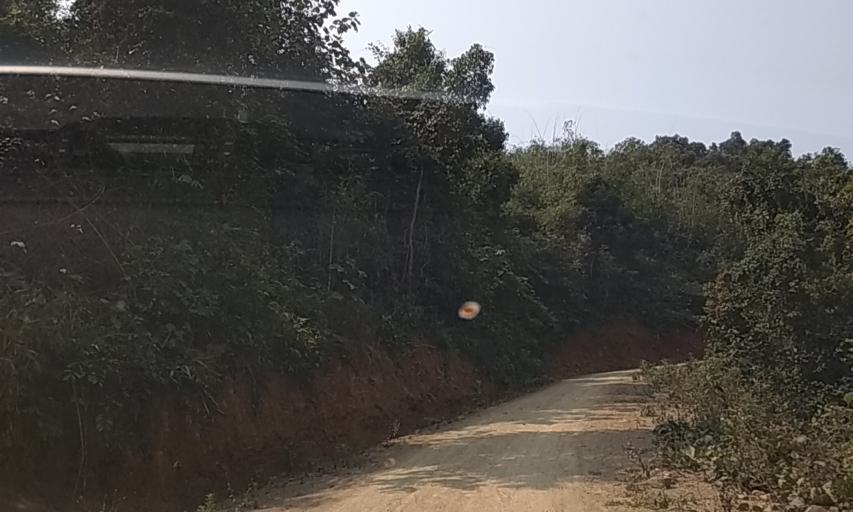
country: LA
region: Phongsali
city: Phongsali
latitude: 21.4714
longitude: 102.4289
